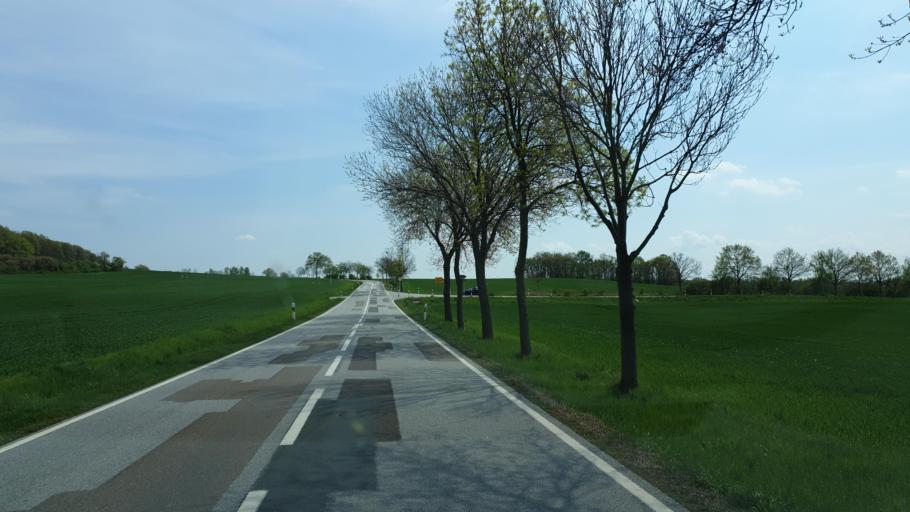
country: DE
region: Saxony
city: Weissenberg
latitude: 51.1821
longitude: 14.6445
